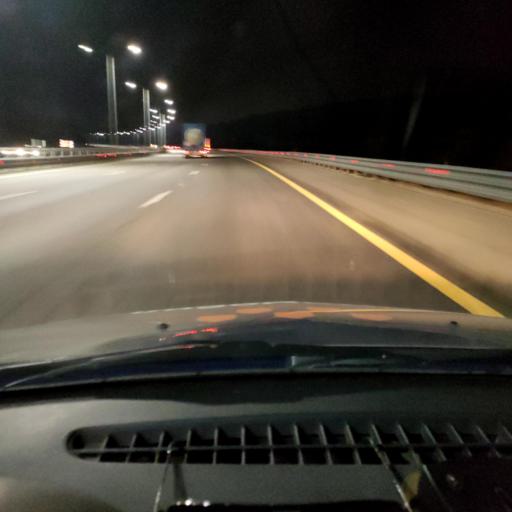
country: RU
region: Voronezj
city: Podgornoye
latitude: 51.8017
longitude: 39.2544
